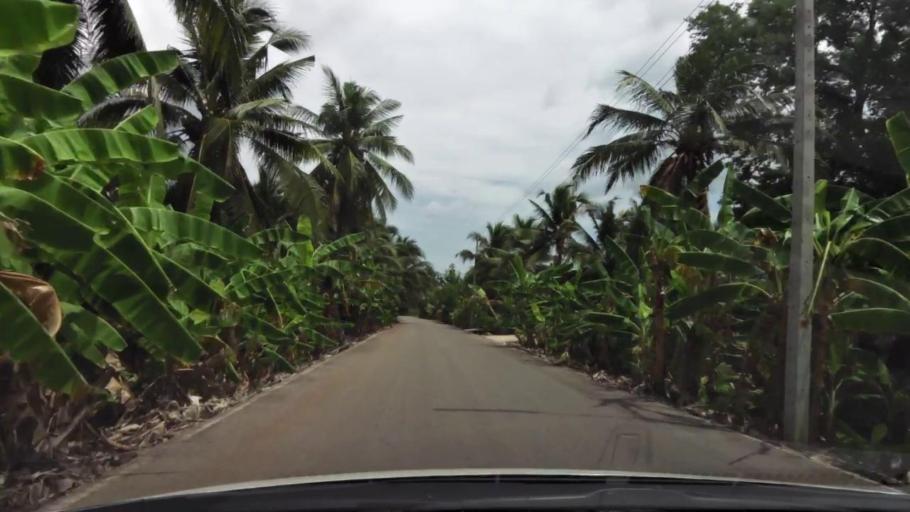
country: TH
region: Ratchaburi
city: Damnoen Saduak
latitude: 13.5335
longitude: 100.0005
